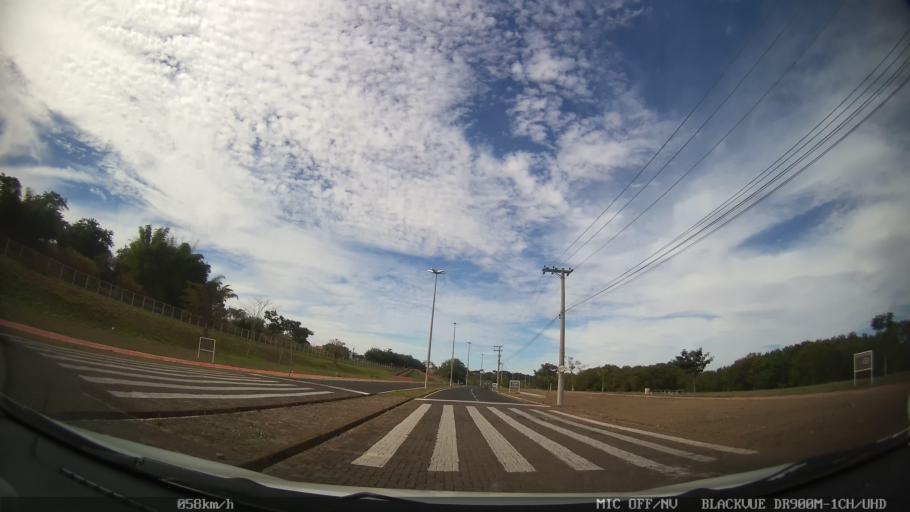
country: BR
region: Sao Paulo
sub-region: Catanduva
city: Catanduva
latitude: -21.1420
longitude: -48.9538
